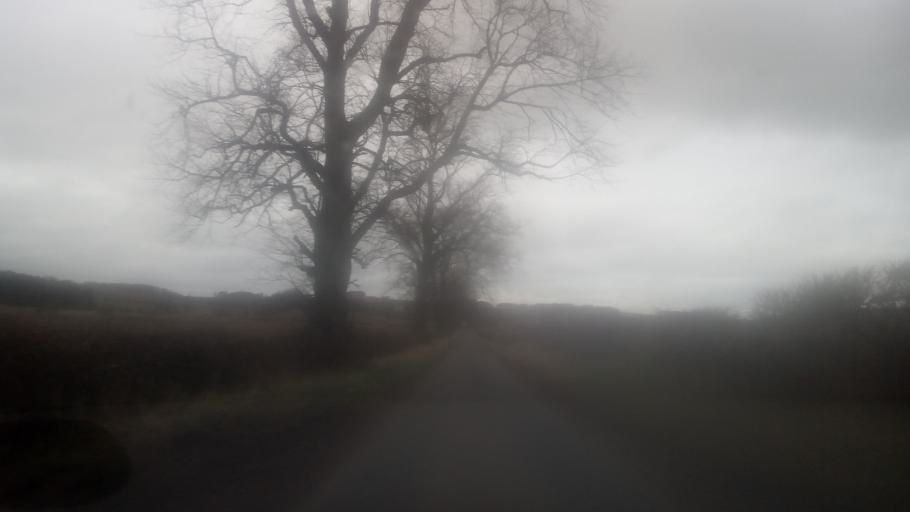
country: GB
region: Scotland
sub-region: The Scottish Borders
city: Jedburgh
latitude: 55.4741
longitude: -2.4850
